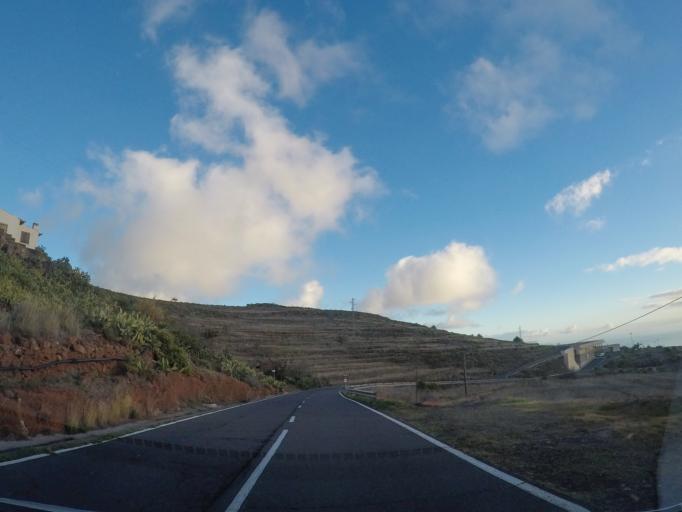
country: ES
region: Canary Islands
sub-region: Provincia de Santa Cruz de Tenerife
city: Alajero
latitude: 28.0721
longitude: -17.2380
